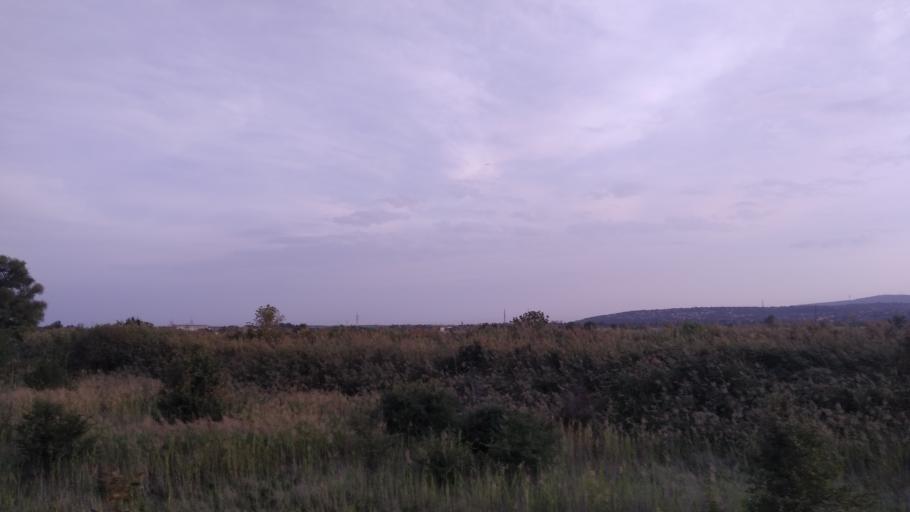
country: HU
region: Pest
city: Szentendre
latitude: 47.6493
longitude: 19.0582
